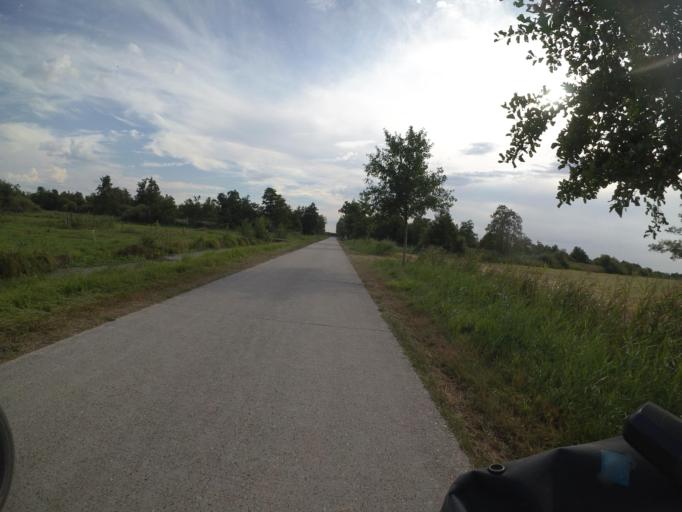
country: NL
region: Overijssel
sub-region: Gemeente Zwartewaterland
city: Hasselt
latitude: 52.6390
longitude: 6.1132
